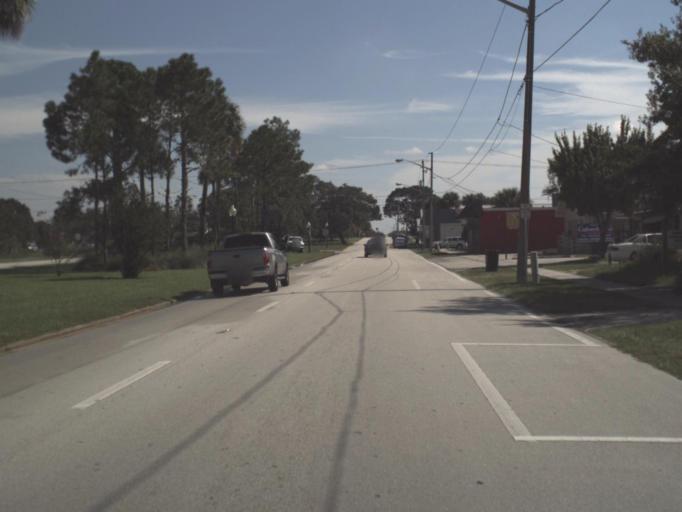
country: US
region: Florida
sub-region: Highlands County
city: Avon Park
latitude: 27.5956
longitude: -81.5116
